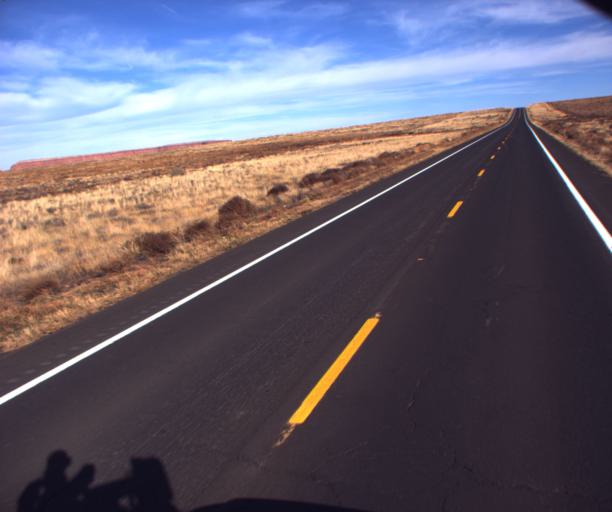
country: US
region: Arizona
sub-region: Apache County
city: Lukachukai
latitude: 36.9618
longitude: -109.4136
